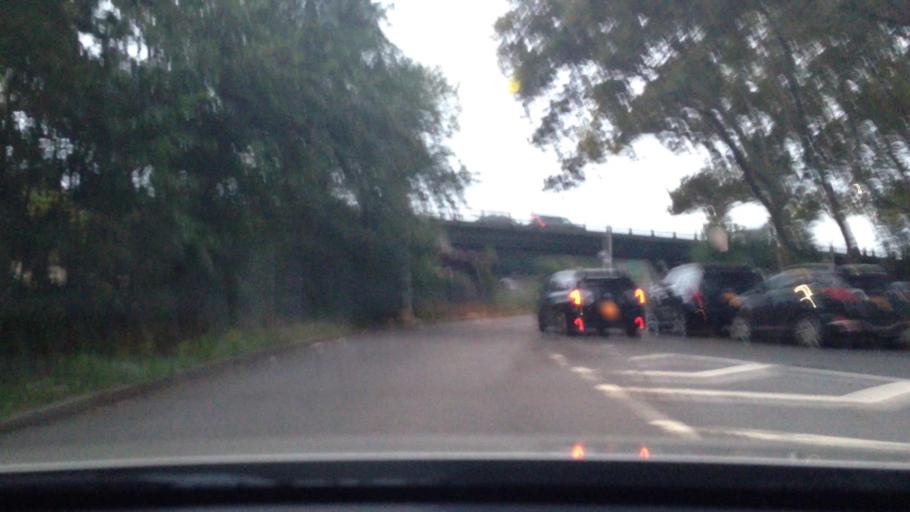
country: US
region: New York
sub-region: New York County
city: Inwood
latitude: 40.8307
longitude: -73.9360
